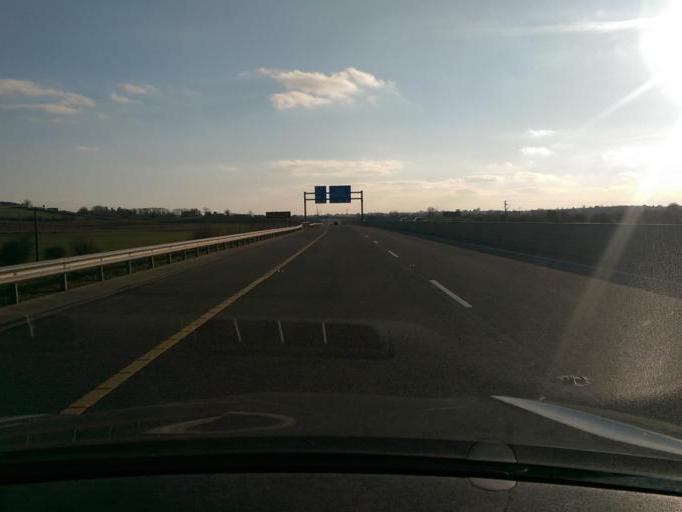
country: IE
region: Leinster
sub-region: Laois
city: Mountrath
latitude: 52.9314
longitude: -7.4688
